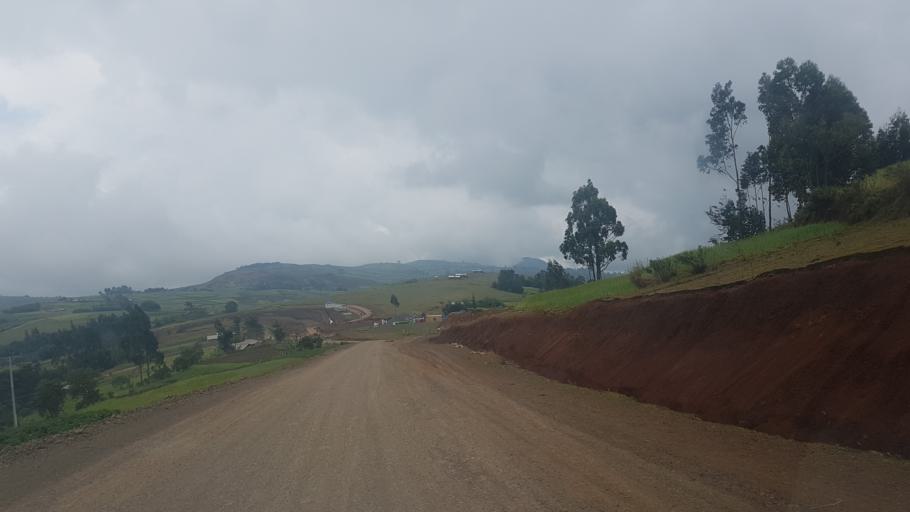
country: ET
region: Southern Nations, Nationalities, and People's Region
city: Arba Minch'
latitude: 6.3240
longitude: 37.5478
